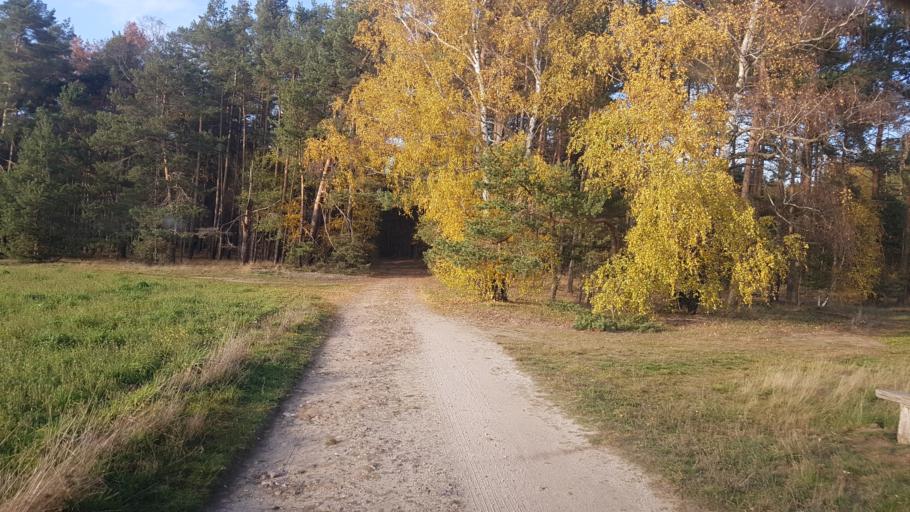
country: DE
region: Brandenburg
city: Calau
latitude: 51.6996
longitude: 13.9566
